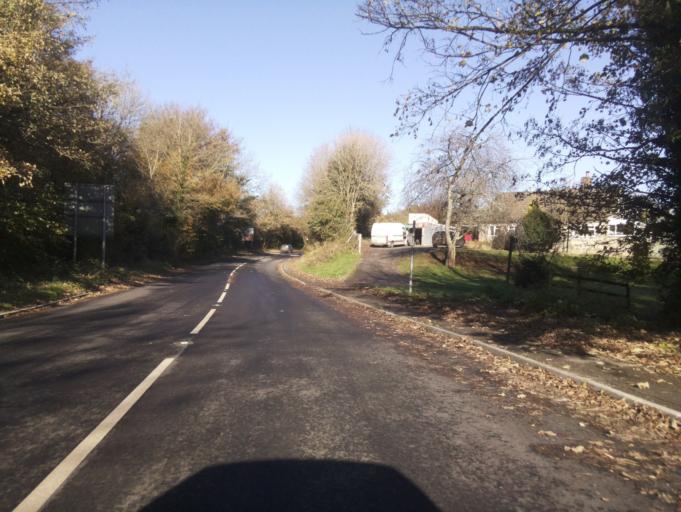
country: GB
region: England
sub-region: Dorset
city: Dorchester
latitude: 50.8105
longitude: -2.4810
